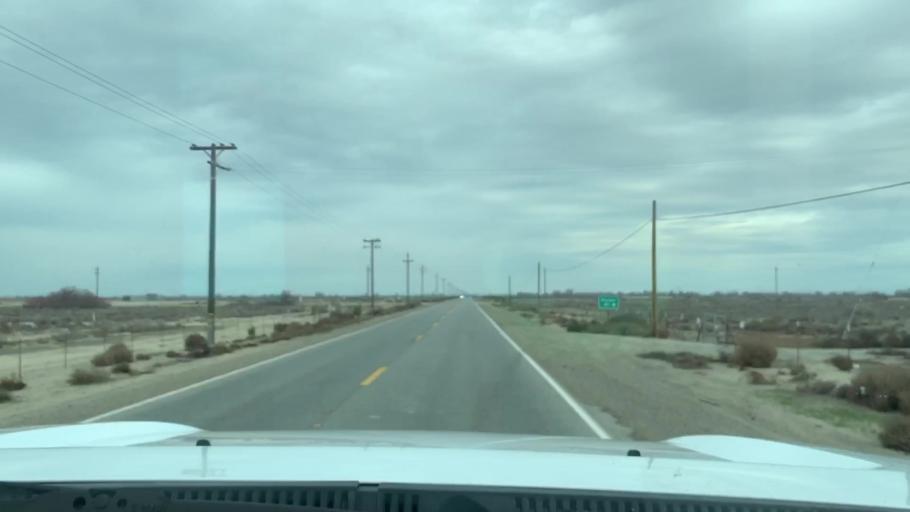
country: US
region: California
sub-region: Kern County
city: Rosedale
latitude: 35.3232
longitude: -119.2524
